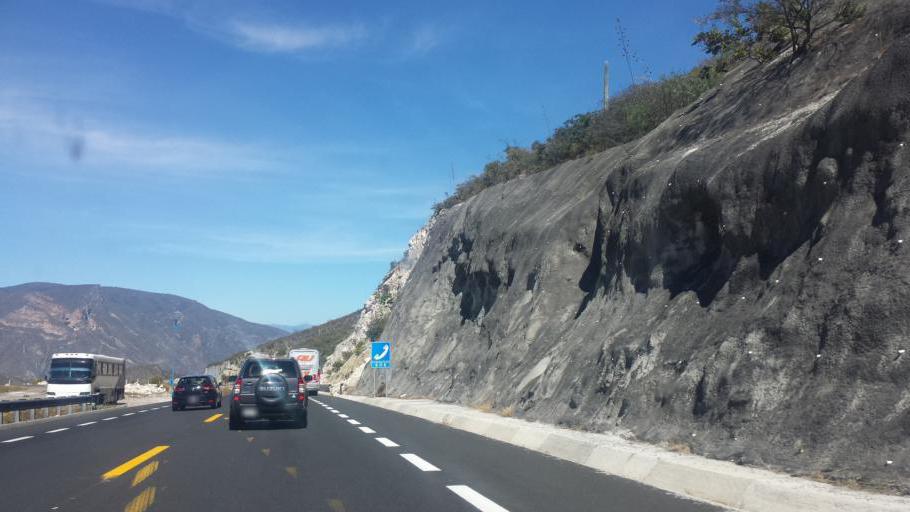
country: MX
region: Puebla
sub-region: San Jose Miahuatlan
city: San Pedro Tetitlan
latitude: 18.0782
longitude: -97.3519
